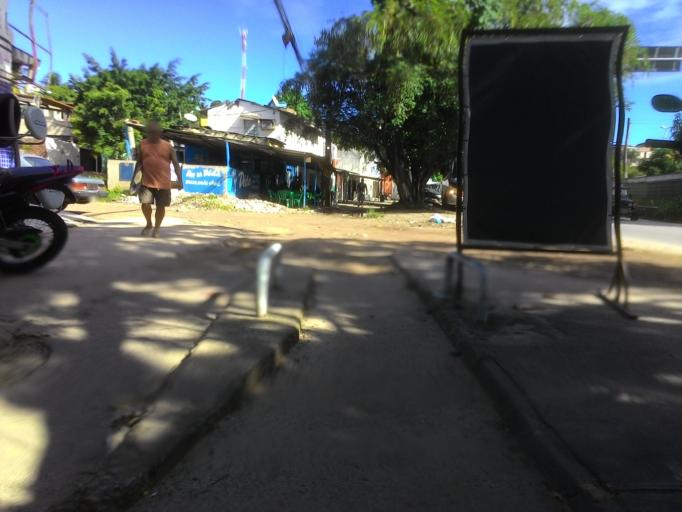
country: BR
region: Pernambuco
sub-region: Olinda
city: Olinda
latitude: -7.9834
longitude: -34.8555
